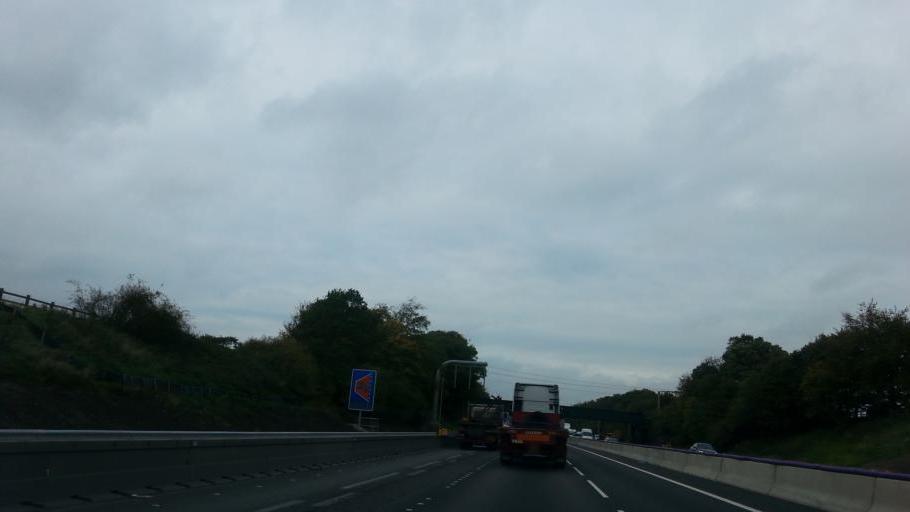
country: GB
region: England
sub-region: Cheshire East
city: Holmes Chapel
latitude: 53.1803
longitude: -2.3673
